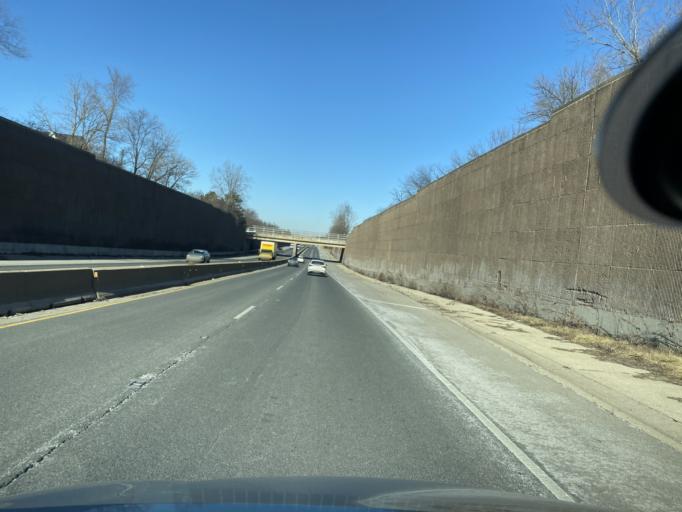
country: US
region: Illinois
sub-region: DuPage County
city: Clarendon Hills
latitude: 41.8018
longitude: -87.9464
